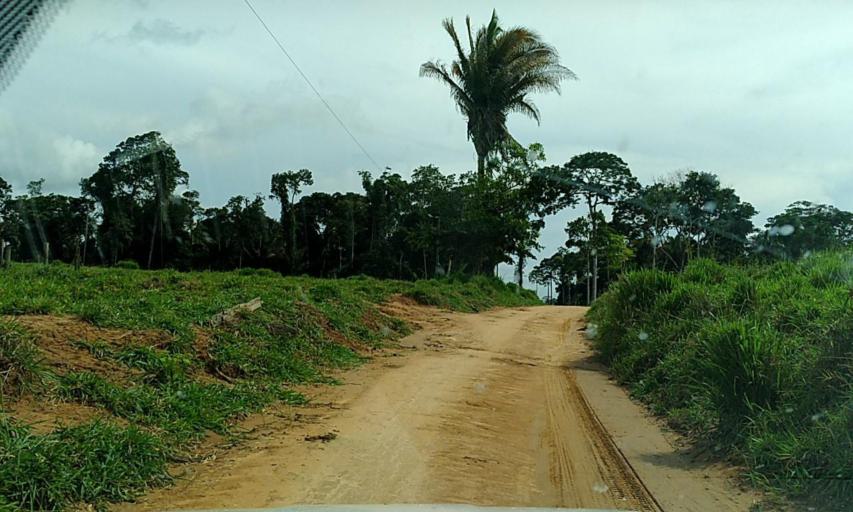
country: BR
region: Para
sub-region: Altamira
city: Altamira
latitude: -3.2328
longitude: -52.7456
